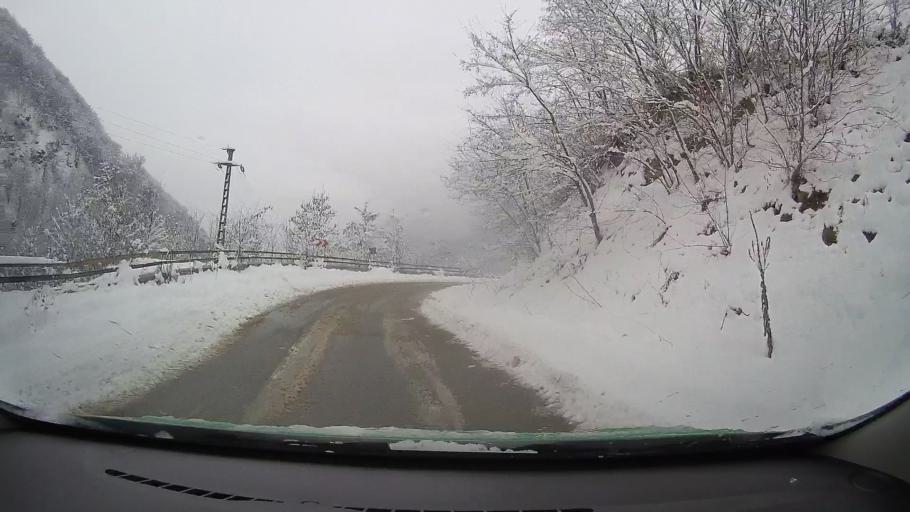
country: RO
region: Alba
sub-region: Comuna Sugag
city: Dobra
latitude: 45.7569
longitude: 23.6636
